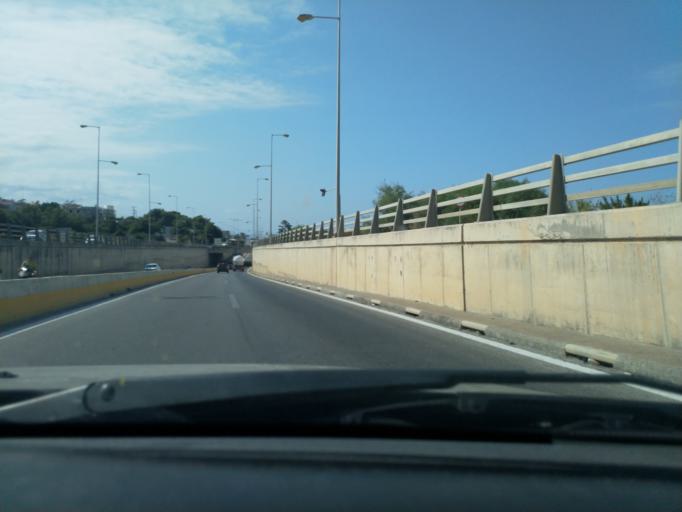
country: GR
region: Crete
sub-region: Nomos Rethymnis
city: Atsipopoulon
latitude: 35.3611
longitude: 24.4466
